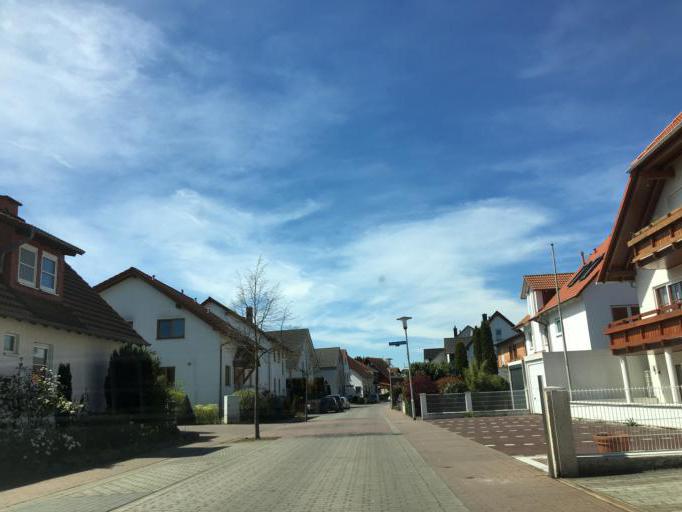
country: DE
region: Hesse
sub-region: Regierungsbezirk Darmstadt
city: Gross-Zimmern
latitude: 49.8656
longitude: 8.8270
